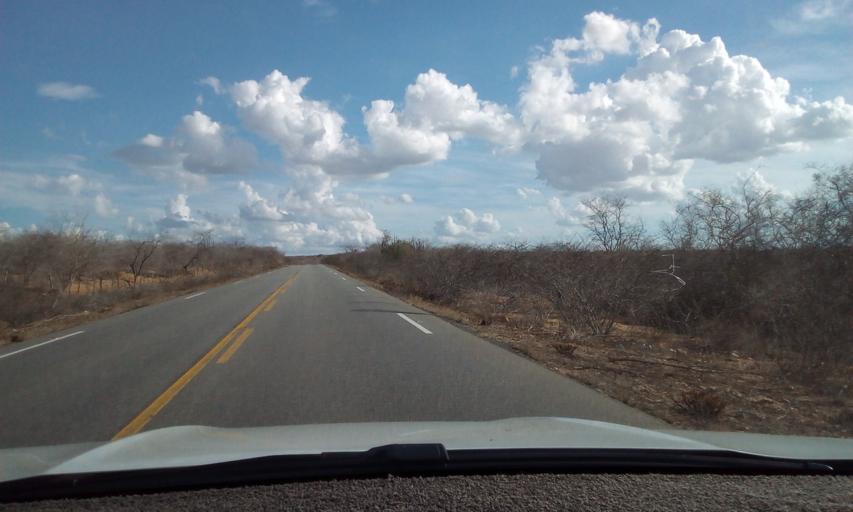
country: BR
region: Paraiba
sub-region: Soledade
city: Soledade
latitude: -6.8716
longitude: -36.4008
